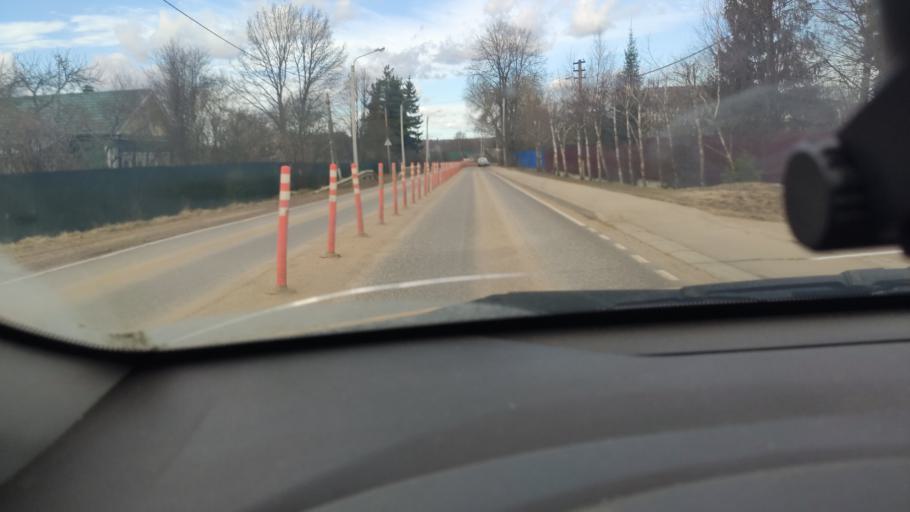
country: RU
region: Moskovskaya
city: Ruza
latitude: 55.7352
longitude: 36.1408
